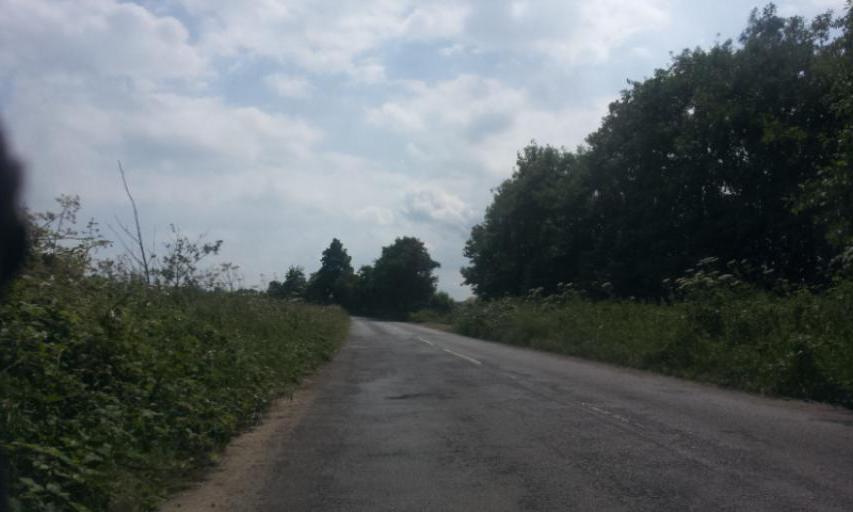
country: GB
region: England
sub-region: Kent
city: Teynham
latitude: 51.2965
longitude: 0.7783
